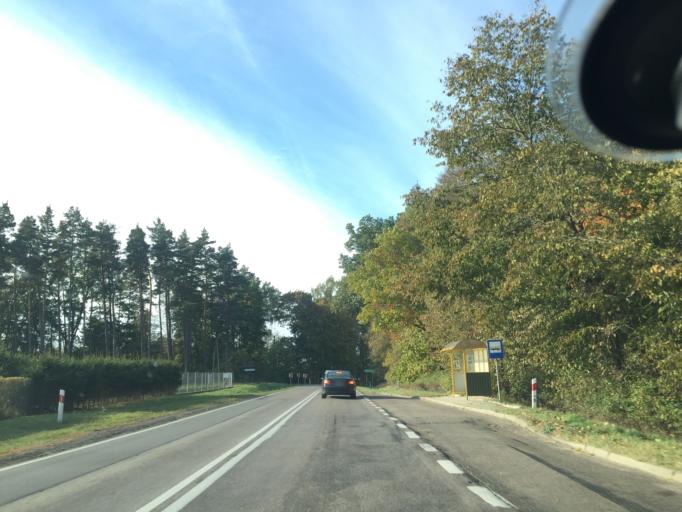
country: PL
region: Warmian-Masurian Voivodeship
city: Dobre Miasto
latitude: 54.0319
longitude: 20.4182
